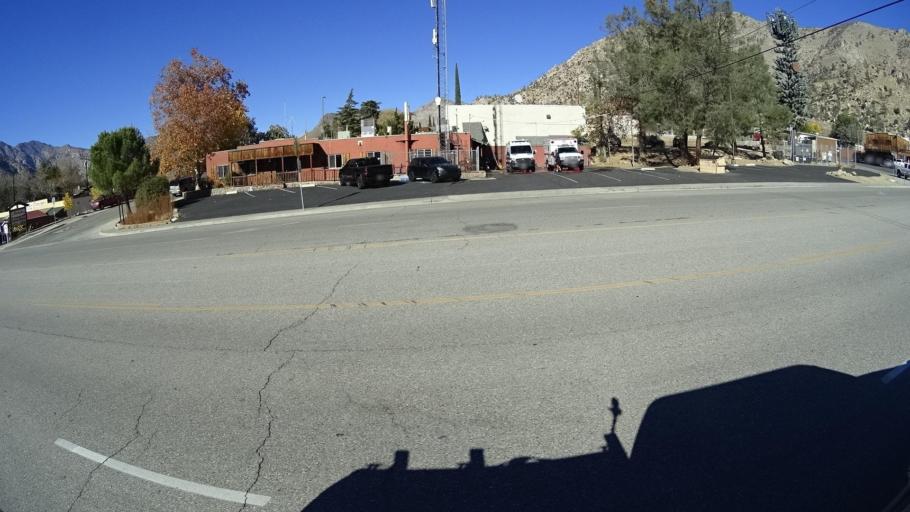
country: US
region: California
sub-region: Kern County
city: Kernville
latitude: 35.7537
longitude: -118.4222
